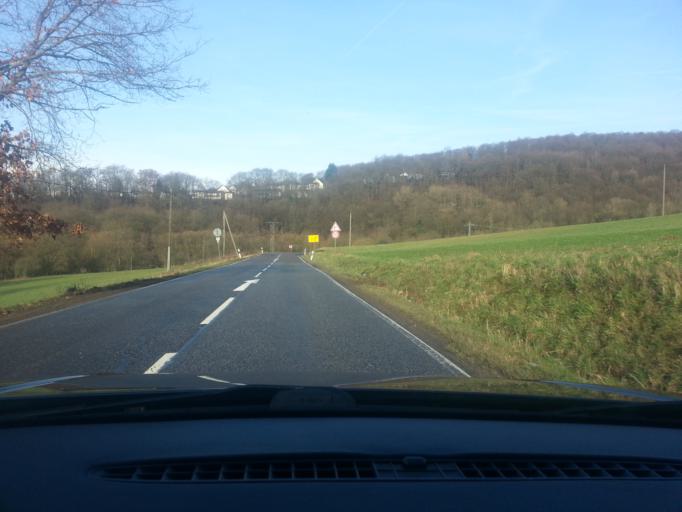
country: DE
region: Rheinland-Pfalz
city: Selchenbach
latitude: 49.4851
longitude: 7.2561
